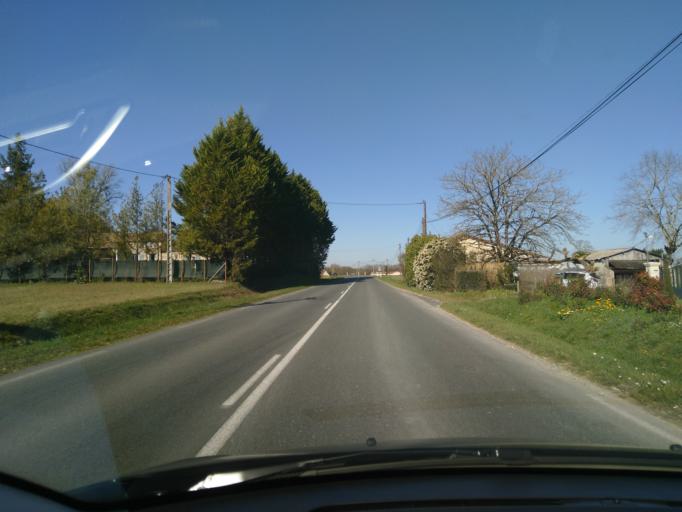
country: FR
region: Aquitaine
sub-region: Departement de la Dordogne
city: Monbazillac
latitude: 44.7477
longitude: 0.5366
